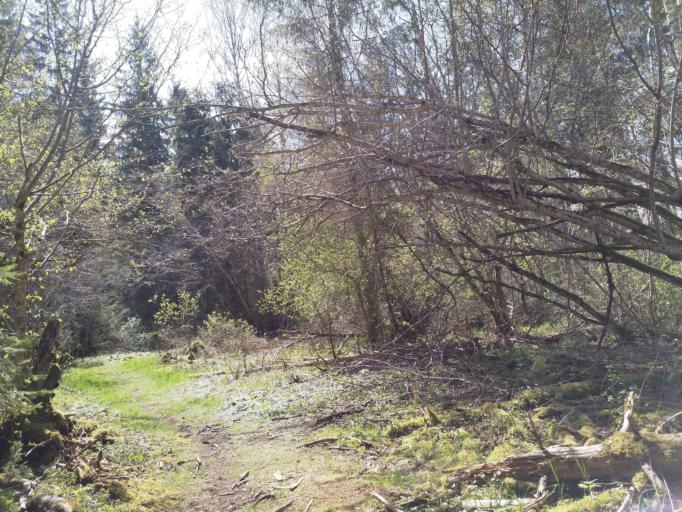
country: LV
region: Kandava
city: Kandava
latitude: 57.0219
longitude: 22.7774
